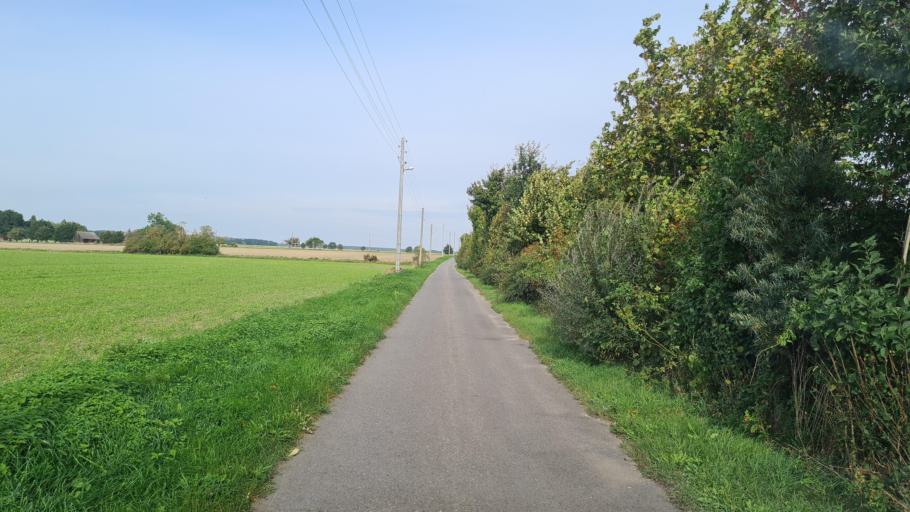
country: DE
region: Brandenburg
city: Sonnewalde
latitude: 51.7160
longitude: 13.6261
